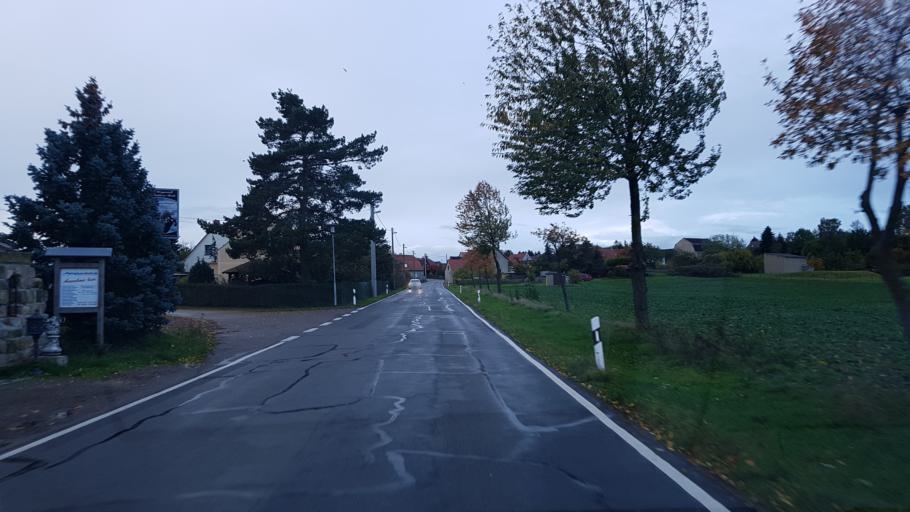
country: DE
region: Saxony
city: Belgern
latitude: 51.4534
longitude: 13.1155
